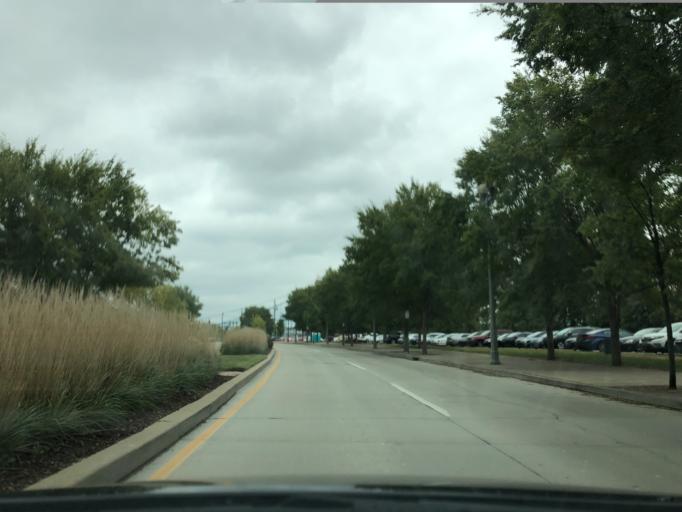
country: US
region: Kentucky
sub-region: Kenton County
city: Covington
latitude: 39.0939
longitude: -84.5161
